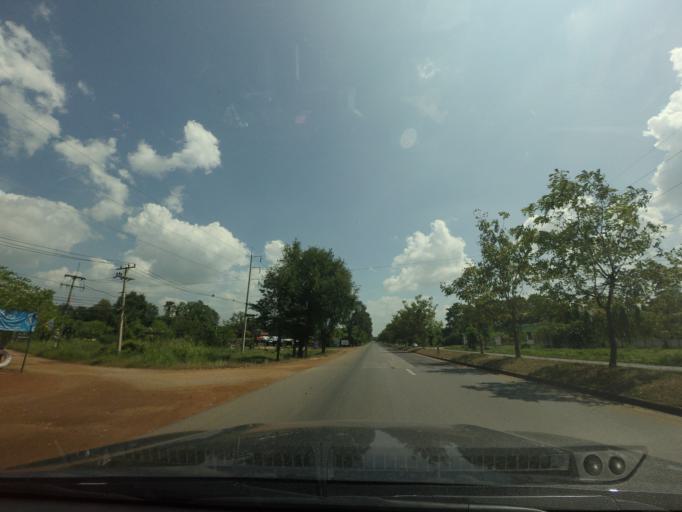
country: TH
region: Phetchabun
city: Nong Phai
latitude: 16.0558
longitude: 101.0761
